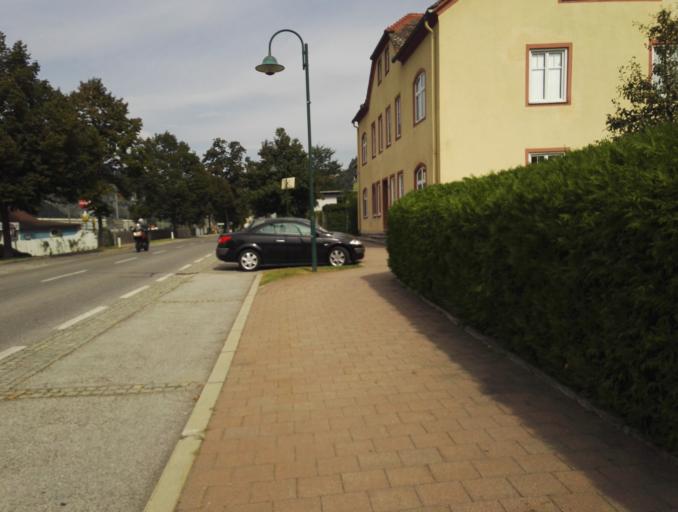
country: AT
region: Styria
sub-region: Politischer Bezirk Graz-Umgebung
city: Peggau
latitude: 47.2072
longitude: 15.3441
